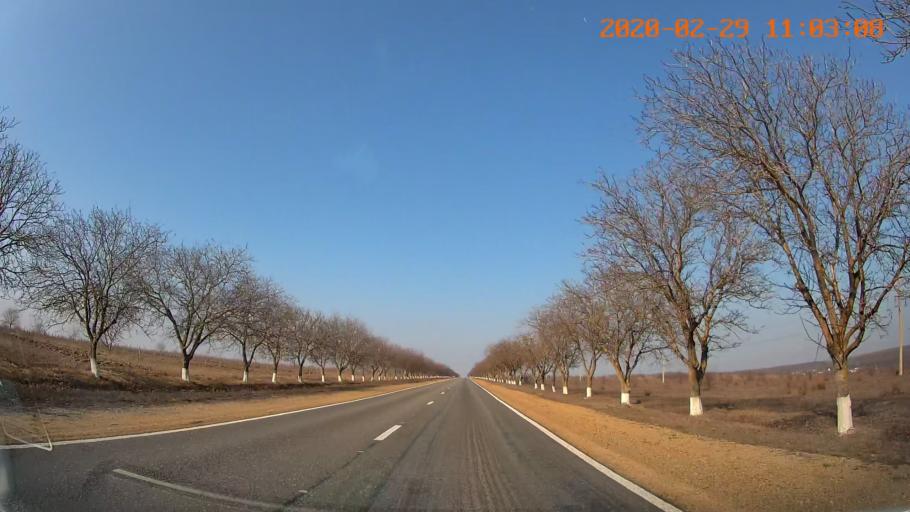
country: MD
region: Criuleni
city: Criuleni
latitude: 47.1774
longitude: 29.2239
